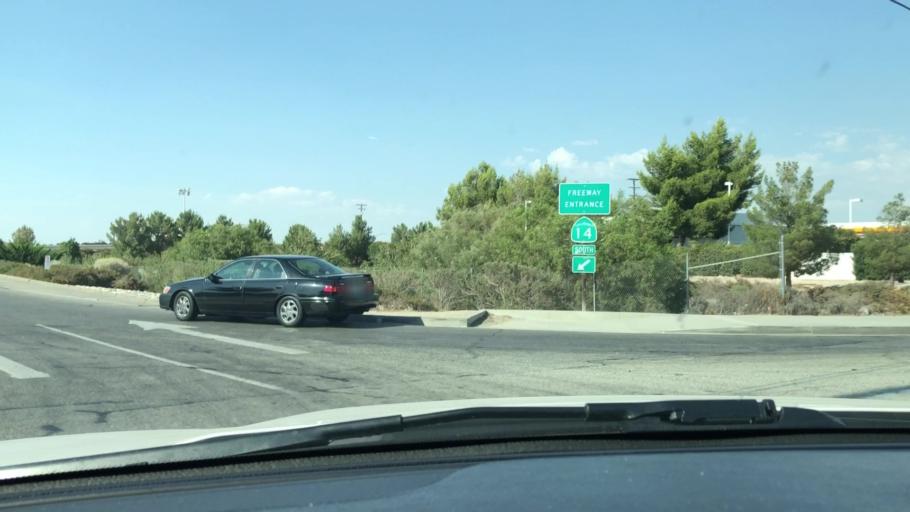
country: US
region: California
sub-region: Los Angeles County
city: Lancaster
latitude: 34.6822
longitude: -118.1672
